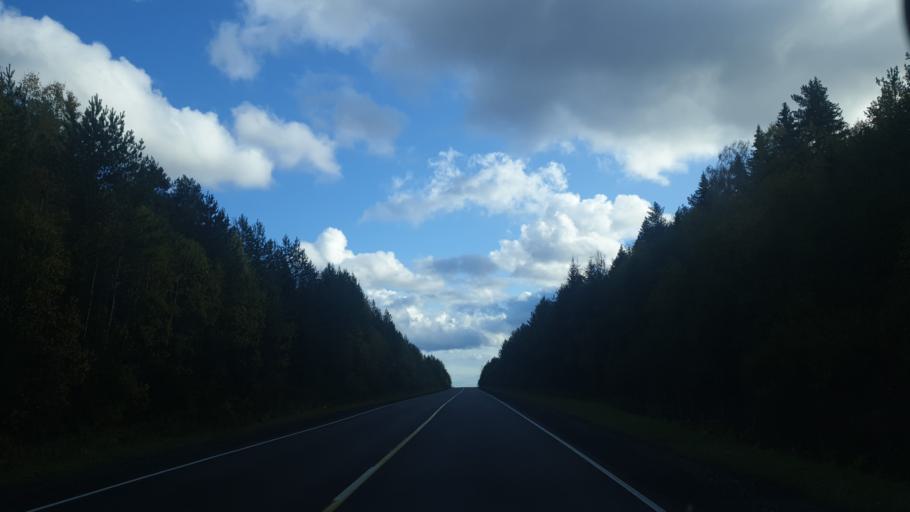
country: RU
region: Komi Republic
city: Letka
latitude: 59.6538
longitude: 49.3972
